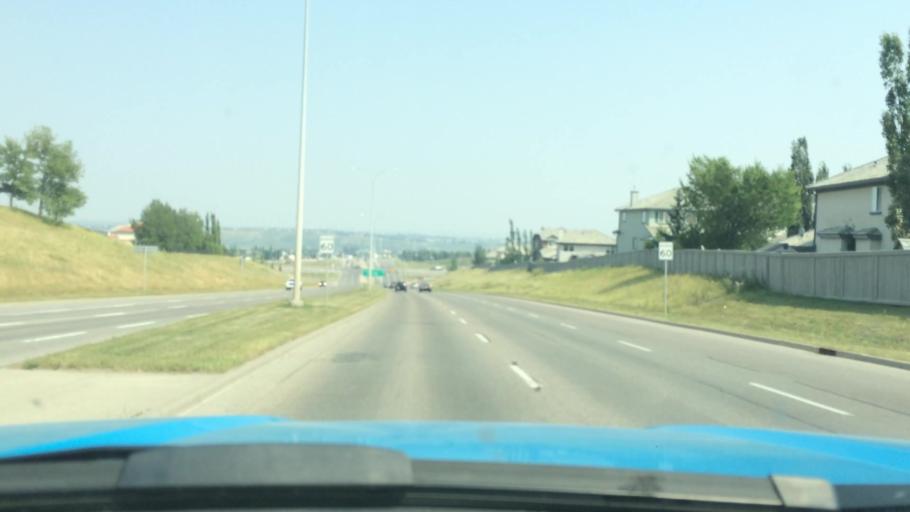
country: CA
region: Alberta
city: Calgary
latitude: 51.1407
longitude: -114.1306
